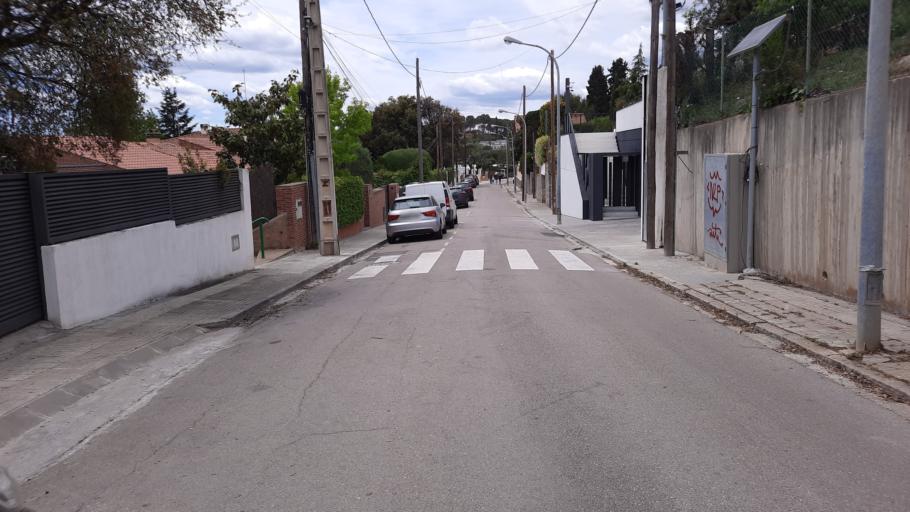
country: ES
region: Catalonia
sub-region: Provincia de Barcelona
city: Sant Quirze del Valles
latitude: 41.5044
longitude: 2.0856
